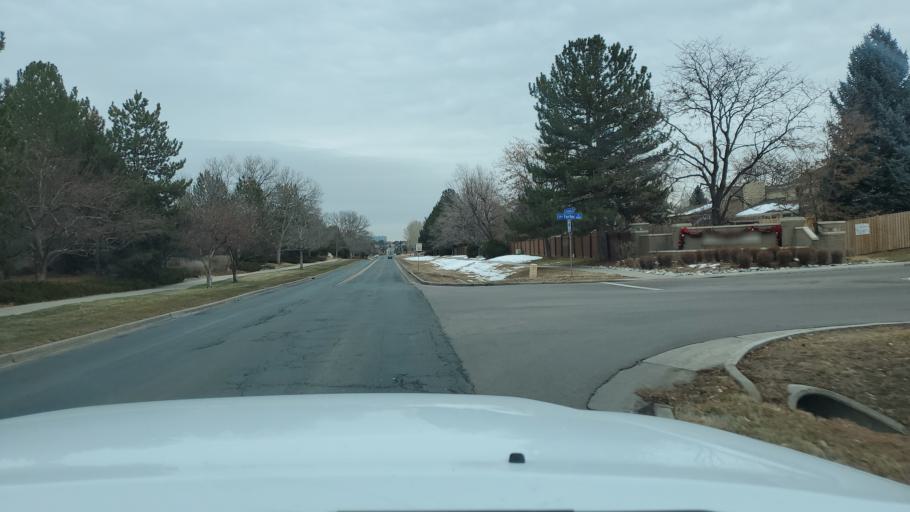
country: US
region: Colorado
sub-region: Arapahoe County
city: Greenwood Village
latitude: 39.6096
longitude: -104.9289
